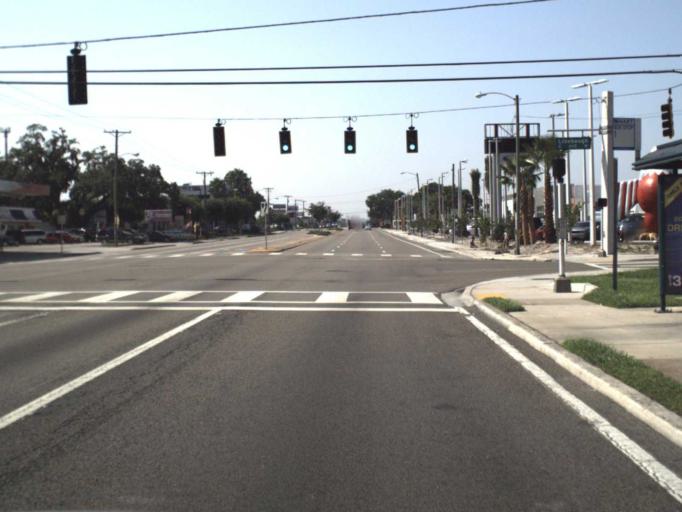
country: US
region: Florida
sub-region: Hillsborough County
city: Carrollwood
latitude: 28.0403
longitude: -82.4595
